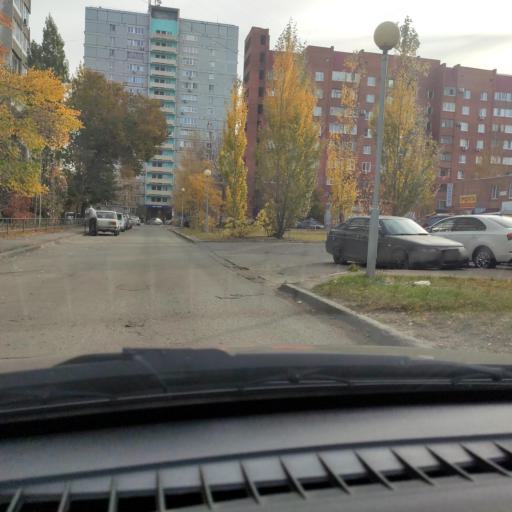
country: RU
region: Samara
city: Tol'yatti
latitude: 53.5360
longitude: 49.3358
